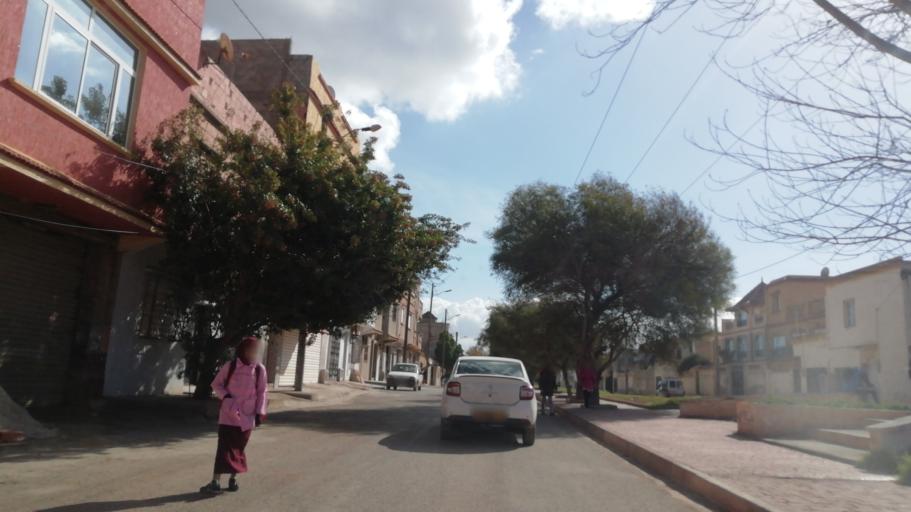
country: DZ
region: Oran
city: Es Senia
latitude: 35.6213
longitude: -0.5822
